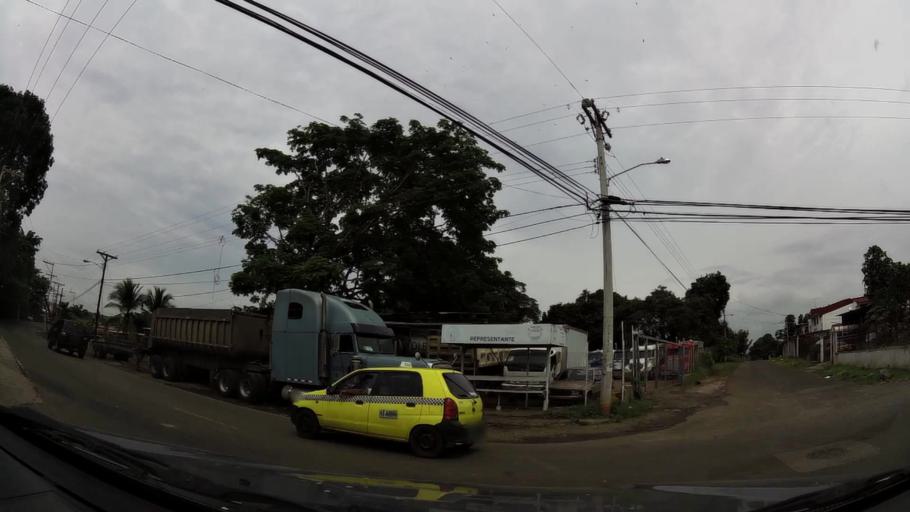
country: PA
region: Panama
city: San Miguelito
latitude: 9.0466
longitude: -79.4342
